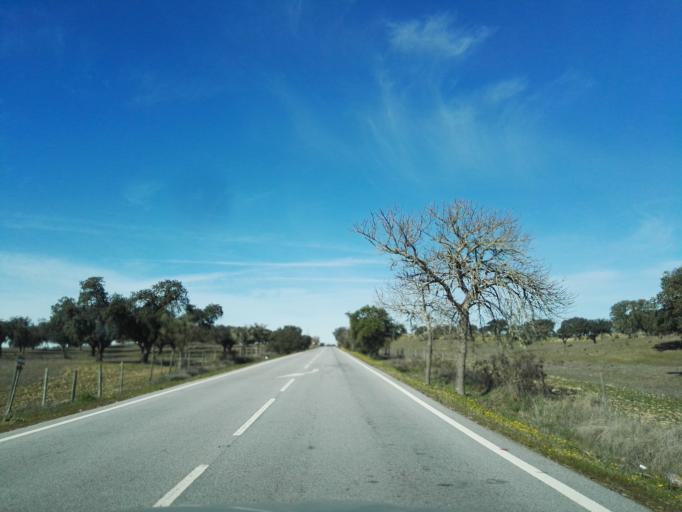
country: PT
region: Portalegre
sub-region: Arronches
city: Arronches
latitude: 39.0763
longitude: -7.2783
